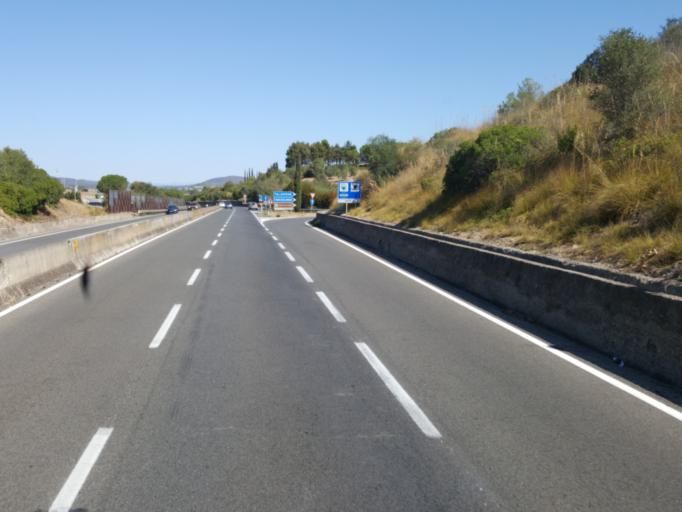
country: IT
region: Tuscany
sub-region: Provincia di Grosseto
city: Fonteblanda
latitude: 42.5649
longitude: 11.1732
